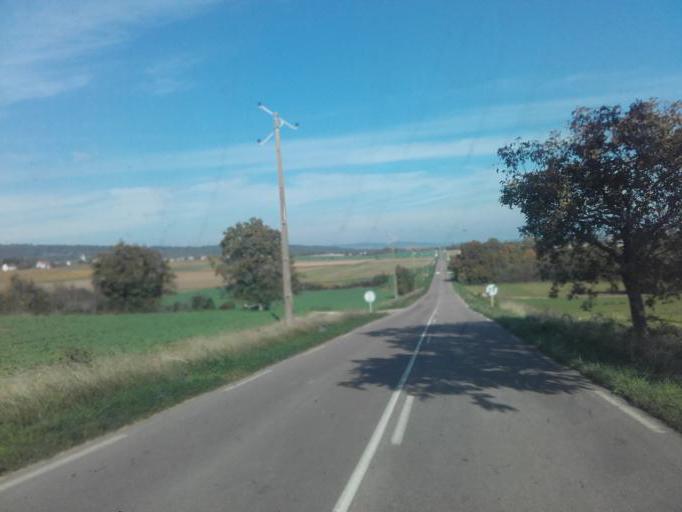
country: FR
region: Bourgogne
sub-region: Departement de Saone-et-Loire
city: Rully
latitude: 46.8591
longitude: 4.7525
